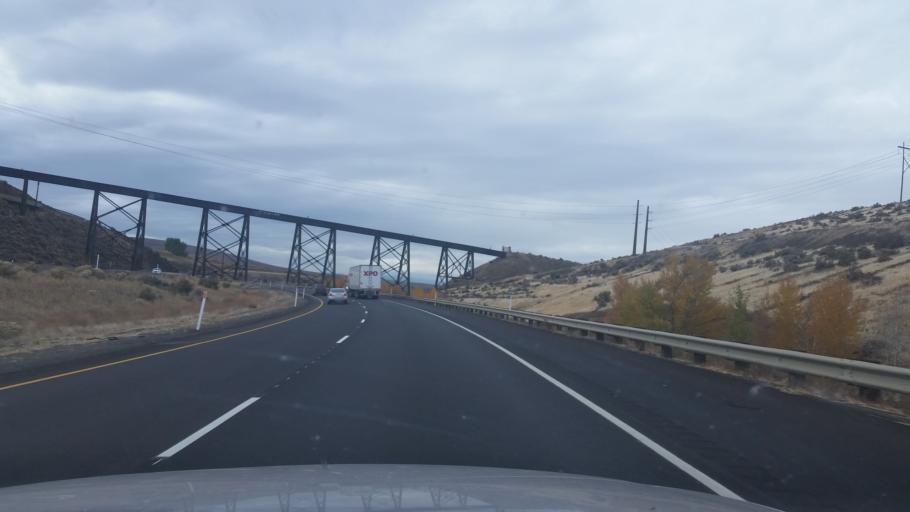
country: US
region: Washington
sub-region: Kittitas County
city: Kittitas
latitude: 46.9566
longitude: -120.2997
